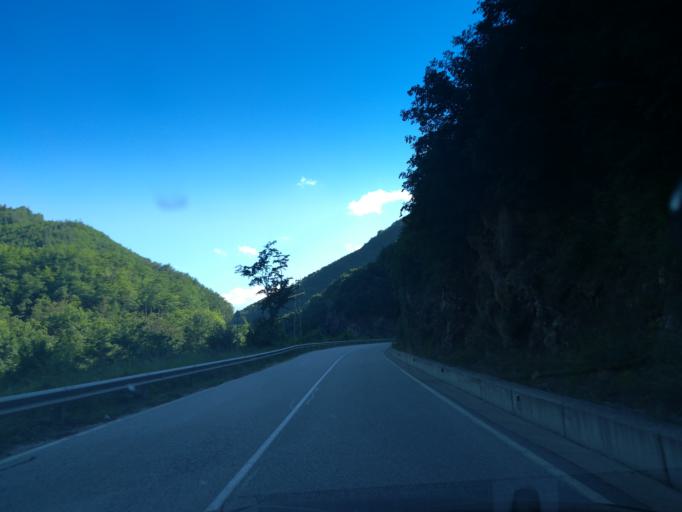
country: BG
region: Smolyan
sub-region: Obshtina Chepelare
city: Chepelare
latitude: 41.7872
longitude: 24.7097
